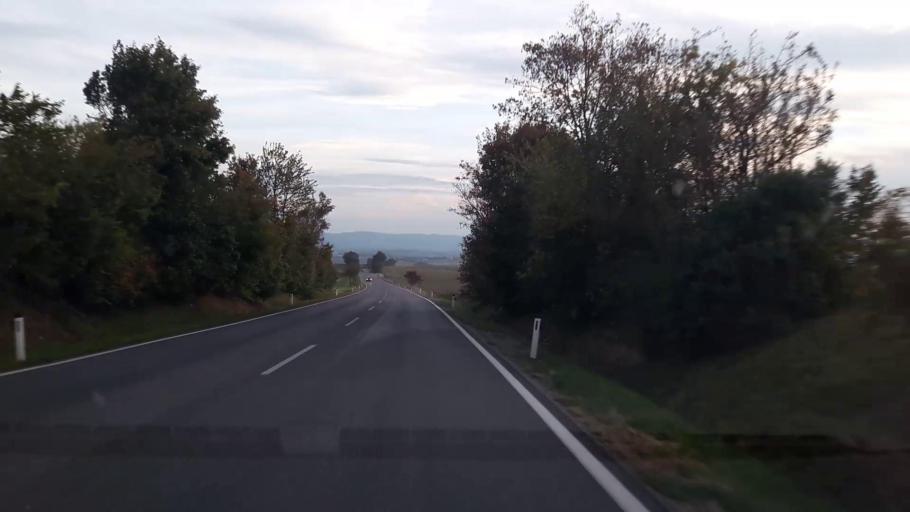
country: AT
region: Lower Austria
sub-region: Politischer Bezirk Korneuburg
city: Grossrussbach
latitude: 48.4300
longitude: 16.3882
